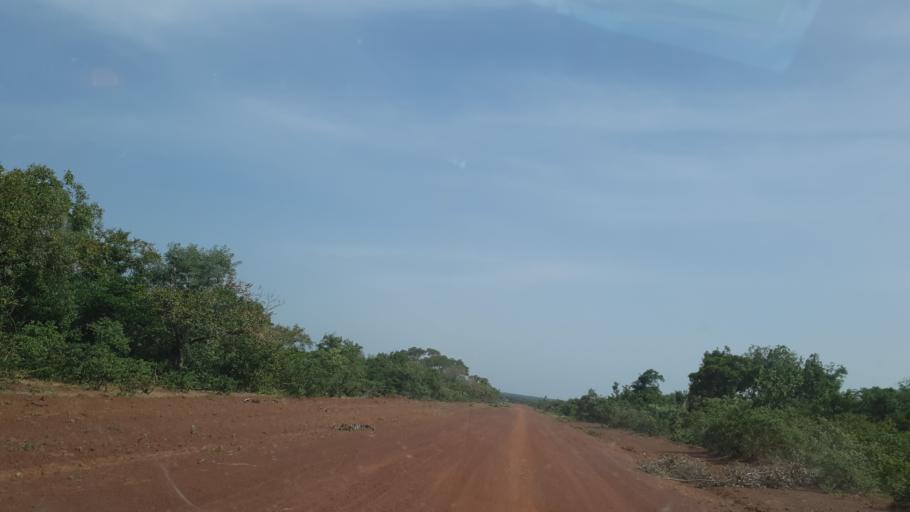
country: ML
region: Koulikoro
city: Dioila
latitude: 12.4654
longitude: -6.1891
